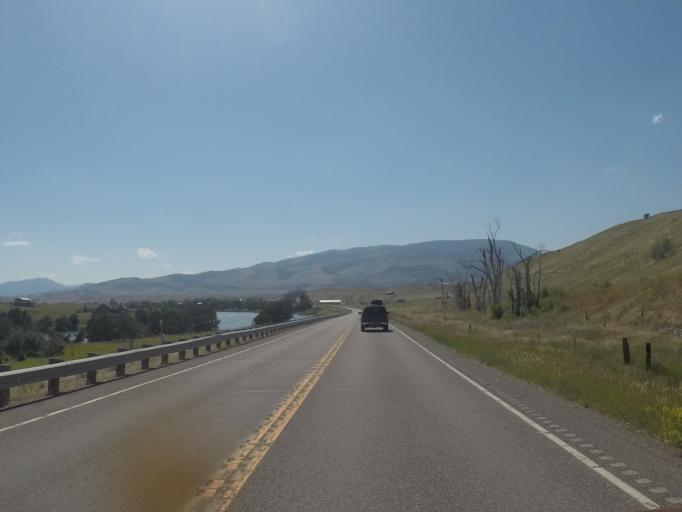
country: US
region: Montana
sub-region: Park County
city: Livingston
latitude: 45.4194
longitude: -110.6724
